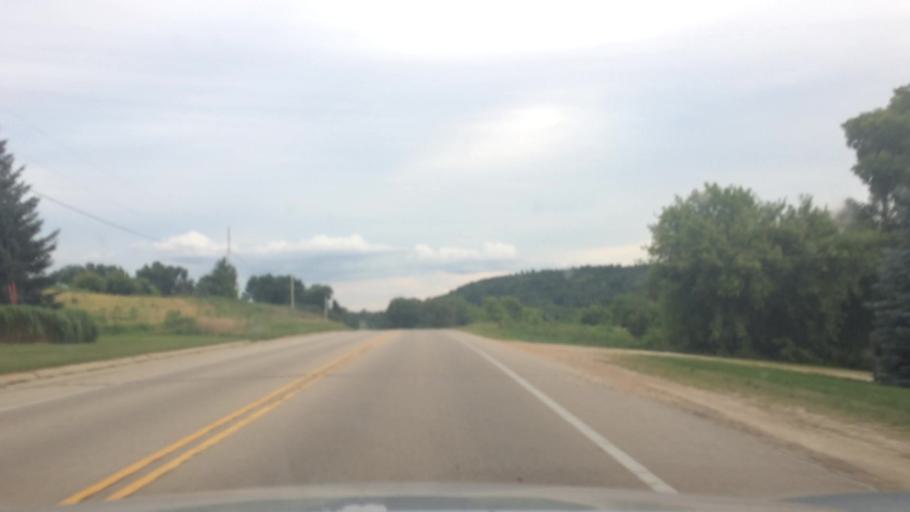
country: US
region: Wisconsin
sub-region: Columbia County
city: Lodi
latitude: 43.3044
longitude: -89.5255
